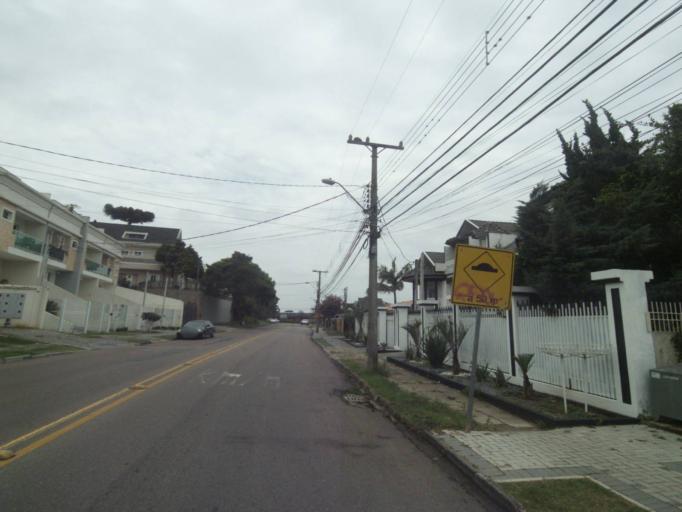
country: BR
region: Parana
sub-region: Curitiba
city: Curitiba
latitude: -25.4098
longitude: -49.2966
